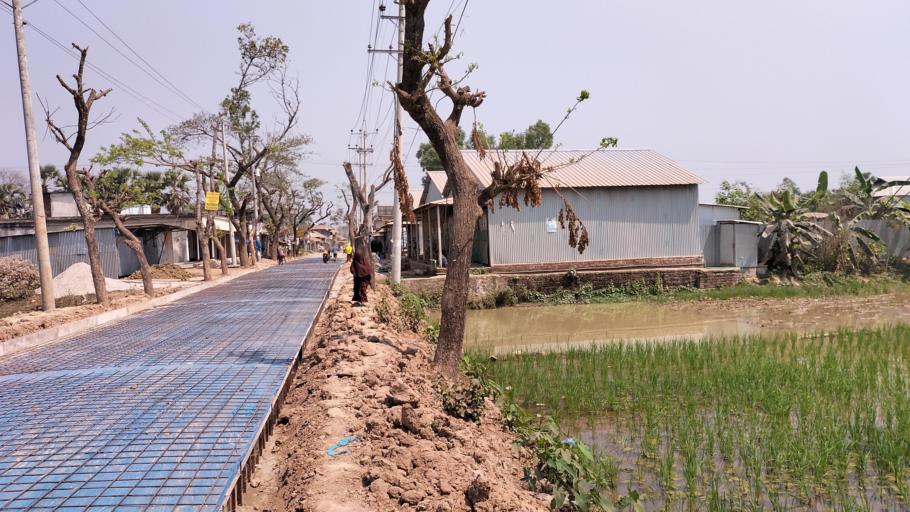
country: BD
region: Dhaka
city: Sakhipur
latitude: 24.3077
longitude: 90.3164
